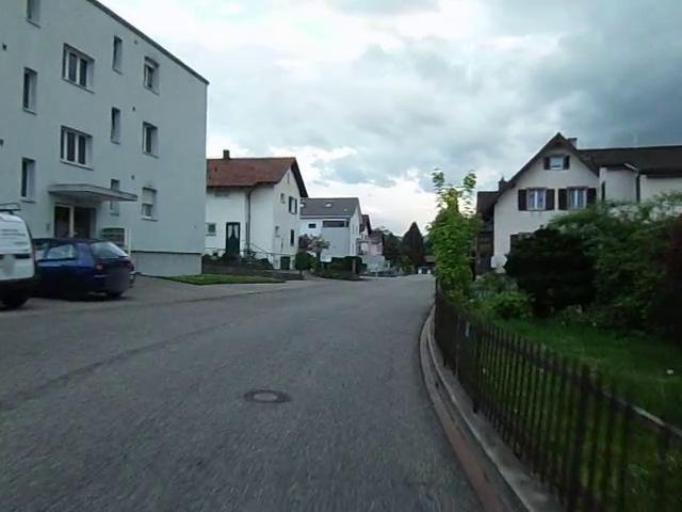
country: CH
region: Zurich
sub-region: Bezirk Hinwil
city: Rueti / Dorfzentrum, Suedl. Teil
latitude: 47.2550
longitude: 8.8581
